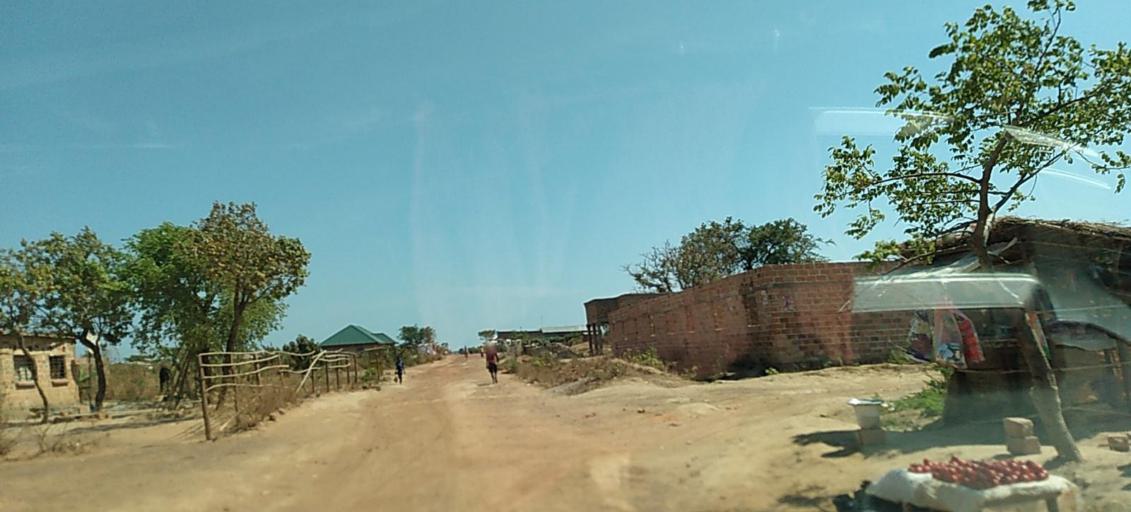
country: ZM
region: Copperbelt
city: Chililabombwe
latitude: -12.3231
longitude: 27.8603
